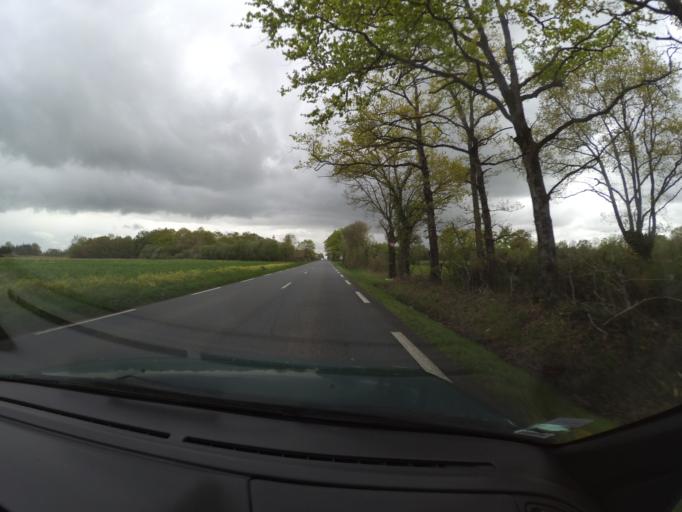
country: FR
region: Pays de la Loire
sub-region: Departement de la Loire-Atlantique
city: La Remaudiere
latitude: 47.2150
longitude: -1.2373
